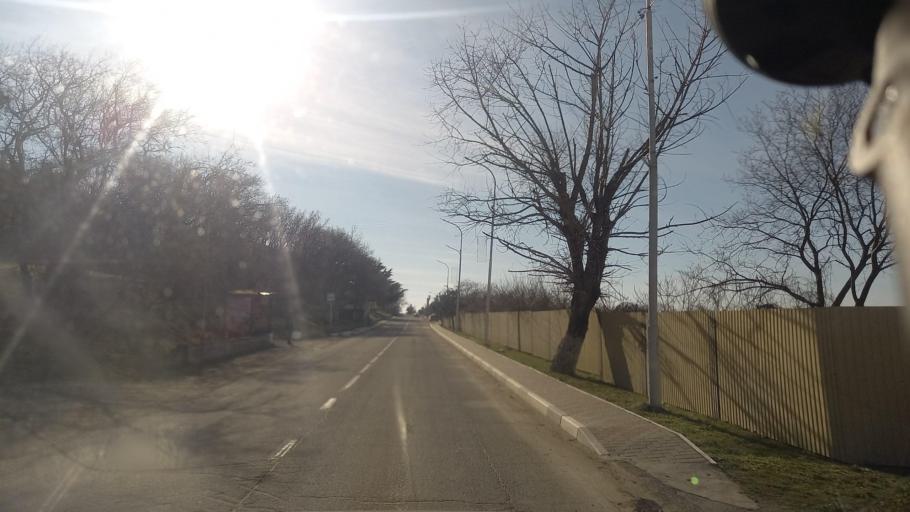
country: RU
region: Krasnodarskiy
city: Kabardinka
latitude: 44.6351
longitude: 37.9145
